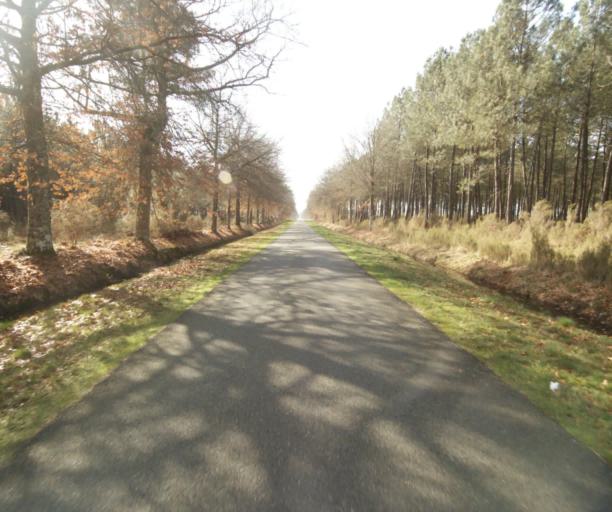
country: FR
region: Aquitaine
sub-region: Departement de la Gironde
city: Grignols
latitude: 44.1950
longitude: -0.1484
